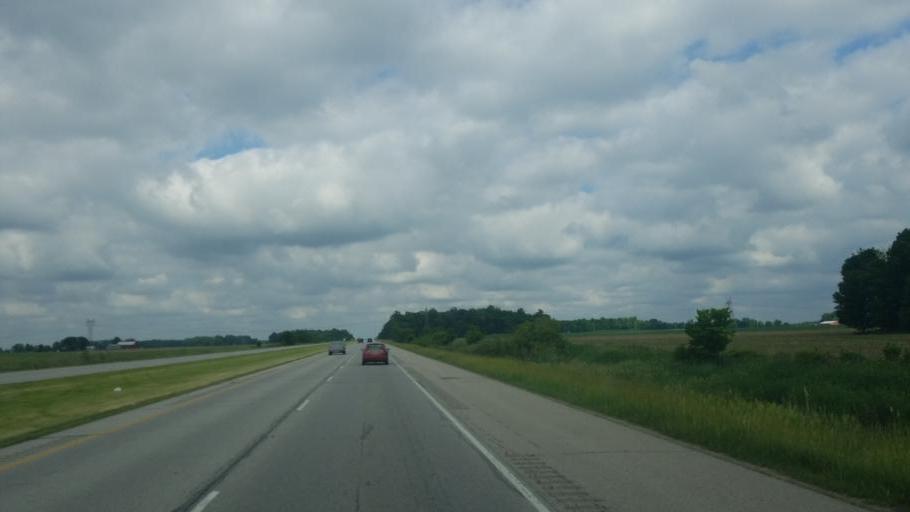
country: US
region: Indiana
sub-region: Kosciusko County
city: Warsaw
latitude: 41.2691
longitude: -85.9252
